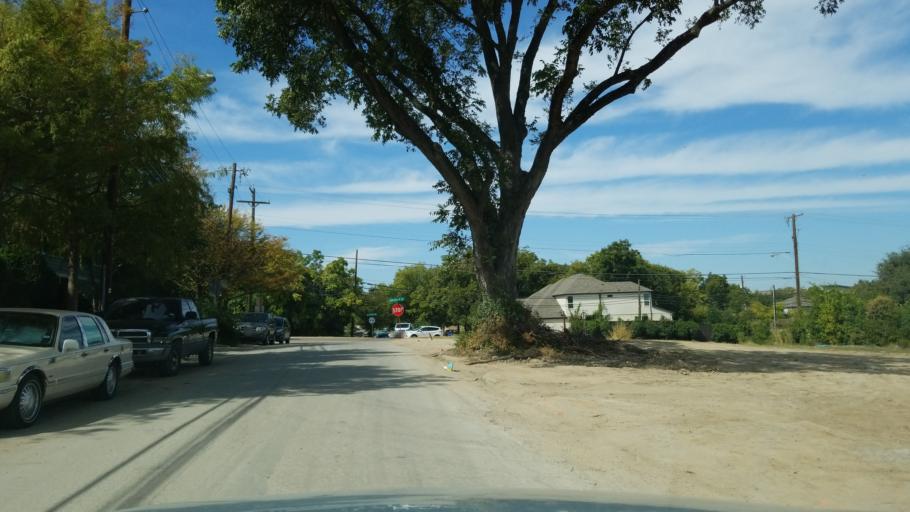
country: US
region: Texas
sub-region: Dallas County
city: Highland Park
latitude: 32.8082
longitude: -96.7313
